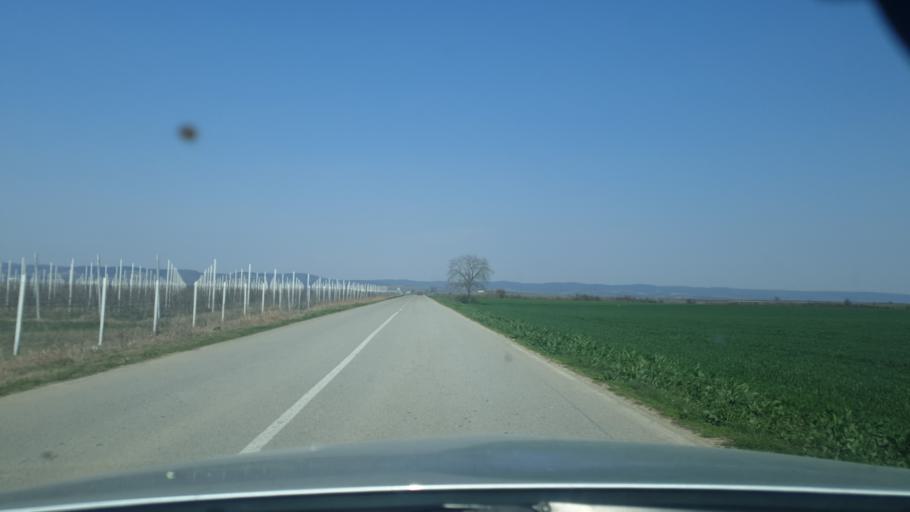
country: RS
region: Autonomna Pokrajina Vojvodina
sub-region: Sremski Okrug
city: Ruma
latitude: 45.0495
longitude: 19.7646
